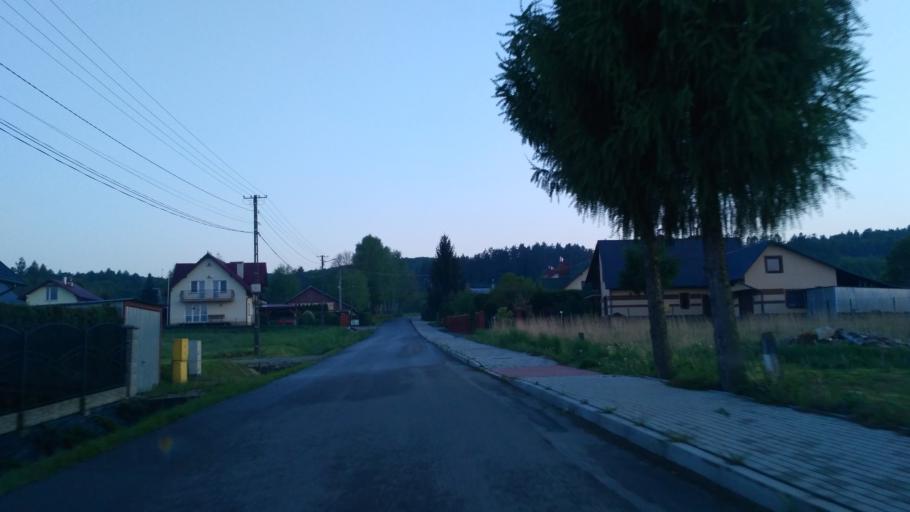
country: PL
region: Subcarpathian Voivodeship
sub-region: Powiat strzyzowski
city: Czudec
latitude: 49.9284
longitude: 21.8514
